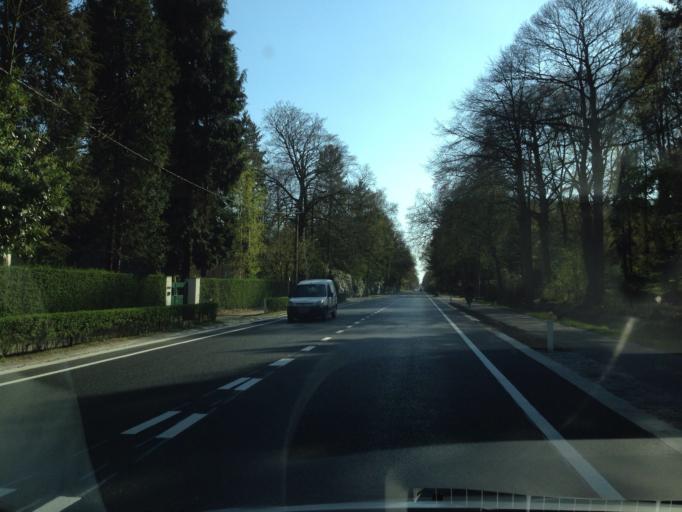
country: BE
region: Flanders
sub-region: Provincie West-Vlaanderen
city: Brugge
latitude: 51.1816
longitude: 3.1865
